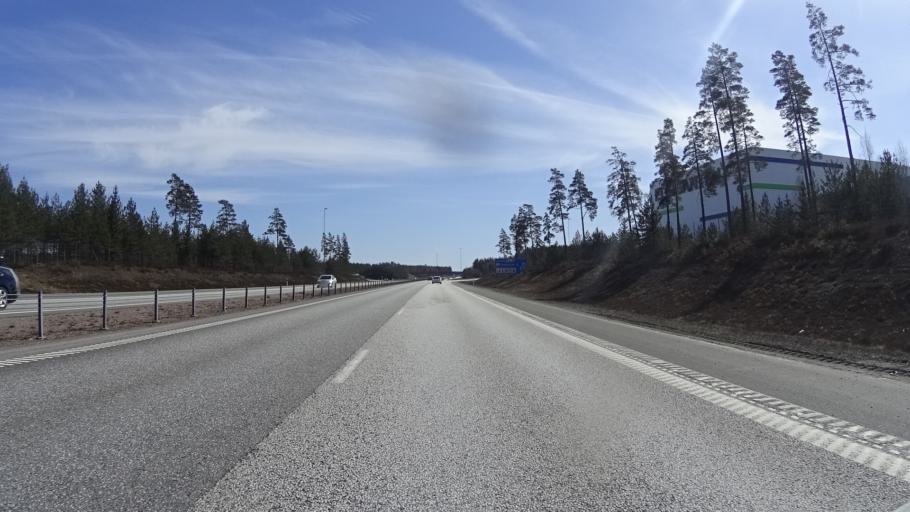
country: SE
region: Joenkoeping
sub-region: Jonkopings Kommun
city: Odensjo
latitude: 57.6719
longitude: 14.1730
